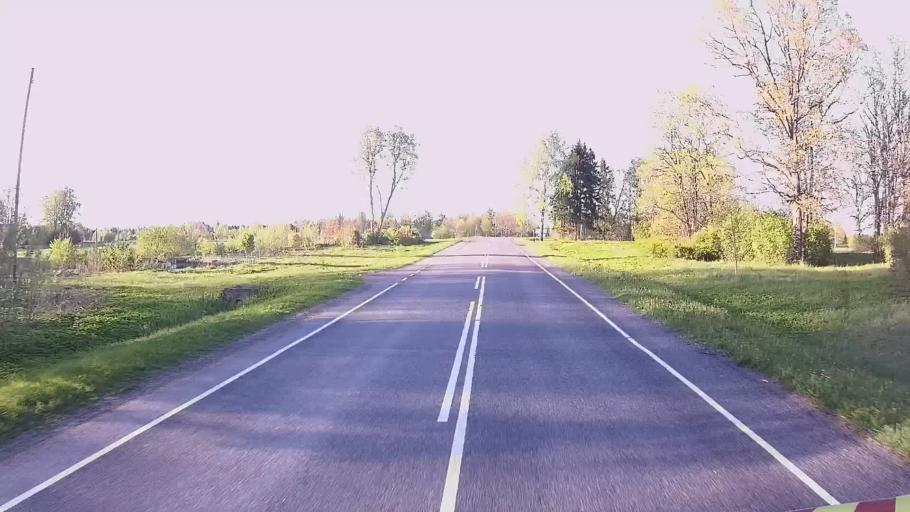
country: EE
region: Jogevamaa
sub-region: Poltsamaa linn
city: Poltsamaa
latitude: 58.5216
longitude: 25.8689
